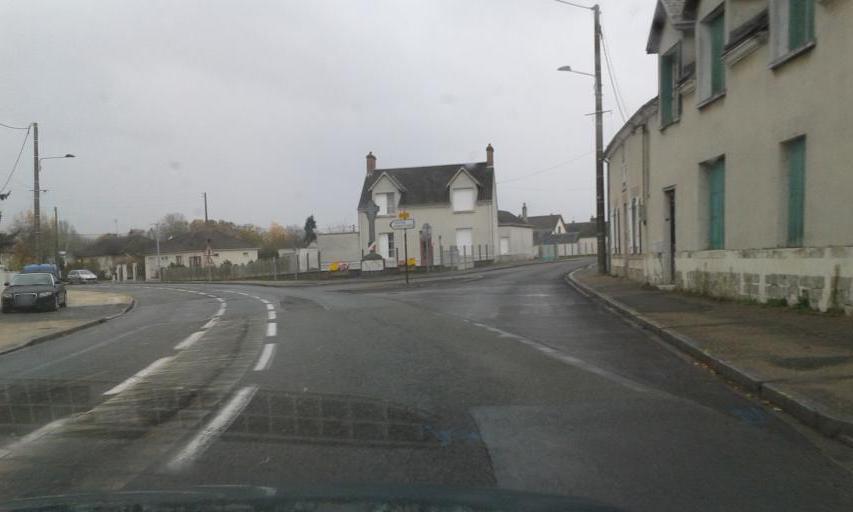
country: FR
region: Centre
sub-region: Departement du Loiret
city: Fay-aux-Loges
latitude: 47.9256
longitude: 2.1362
